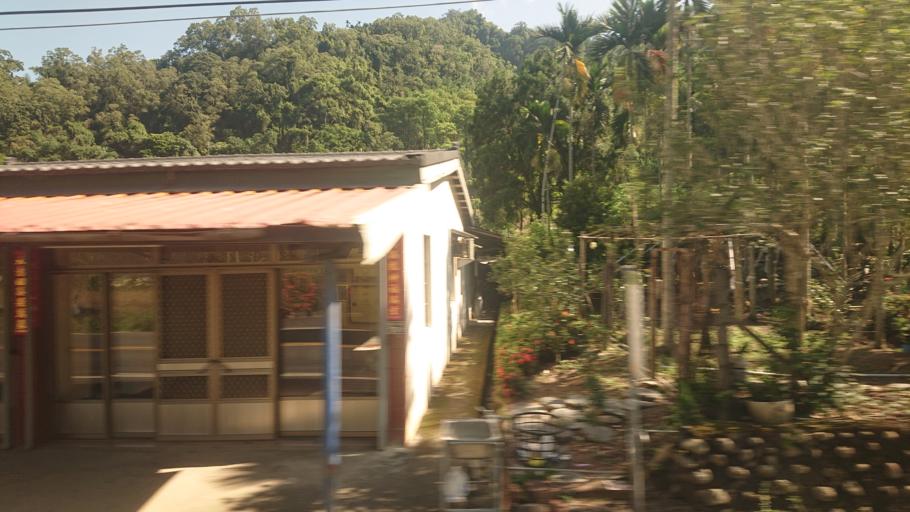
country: TW
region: Taiwan
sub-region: Nantou
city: Puli
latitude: 24.0615
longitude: 120.8908
